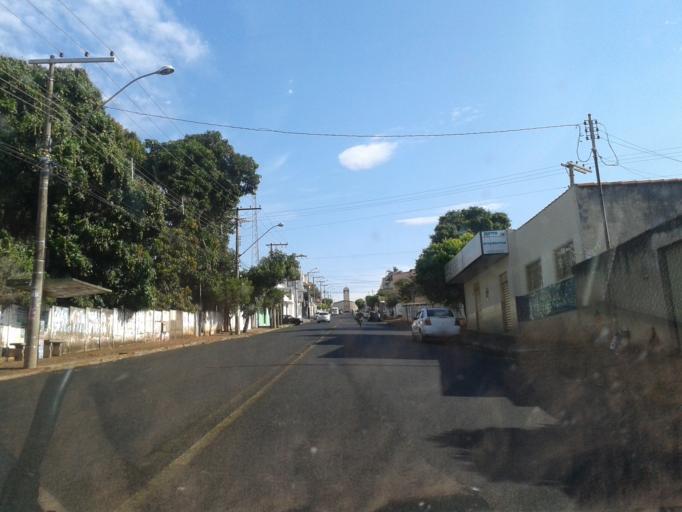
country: BR
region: Minas Gerais
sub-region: Uberlandia
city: Uberlandia
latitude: -18.9341
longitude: -48.2970
